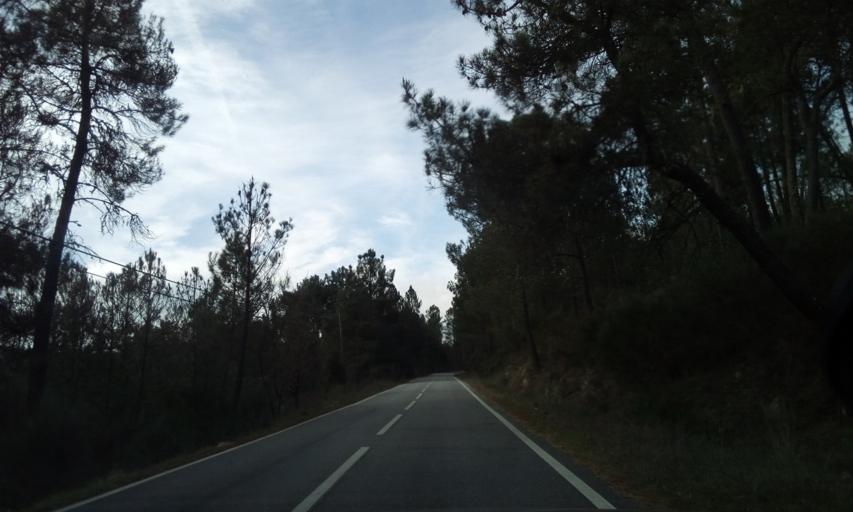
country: PT
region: Guarda
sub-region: Fornos de Algodres
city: Fornos de Algodres
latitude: 40.7125
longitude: -7.5638
